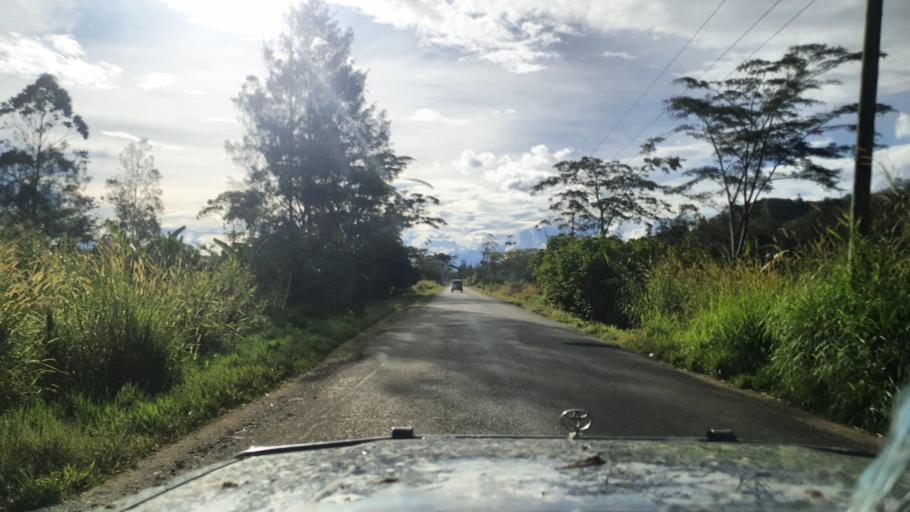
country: PG
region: Jiwaka
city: Minj
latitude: -5.9159
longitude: 144.7632
